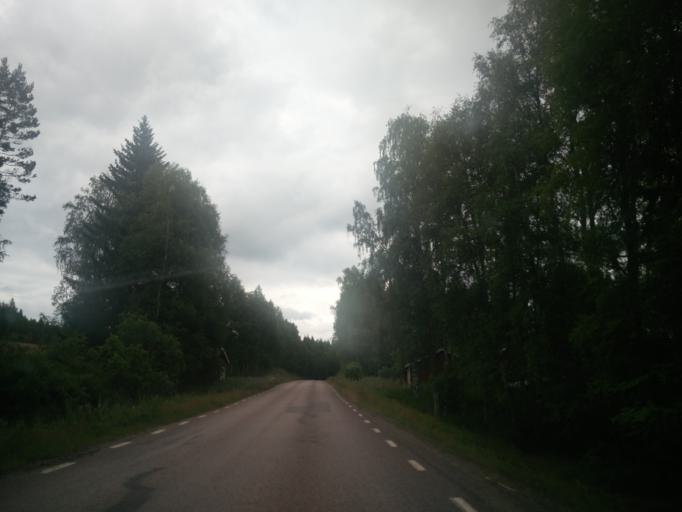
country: SE
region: Vaermland
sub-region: Arvika Kommun
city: Arvika
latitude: 59.9033
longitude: 12.6427
